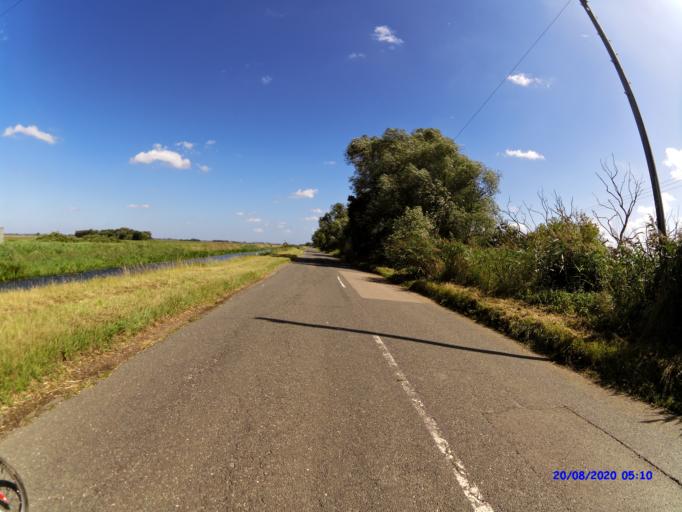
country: GB
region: England
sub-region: Cambridgeshire
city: Whittlesey
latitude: 52.5166
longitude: -0.1307
